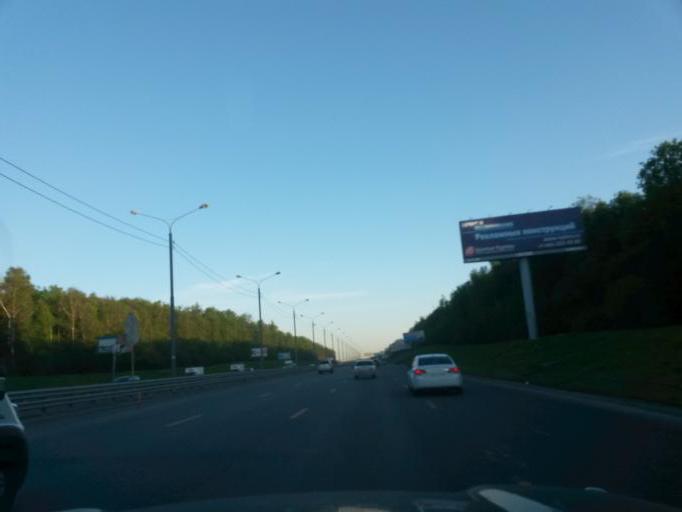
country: RU
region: Moscow
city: Annino
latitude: 55.5543
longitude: 37.6054
